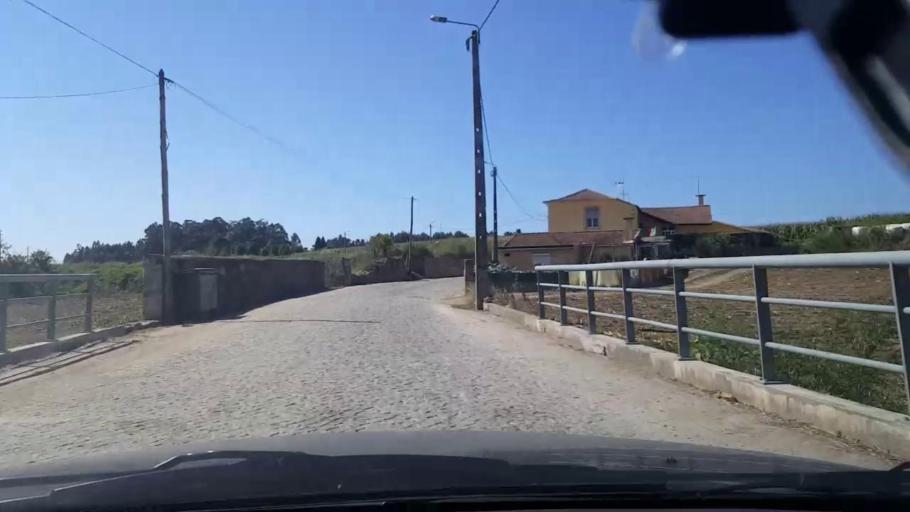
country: PT
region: Porto
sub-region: Matosinhos
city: Lavra
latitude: 41.2855
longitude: -8.6881
